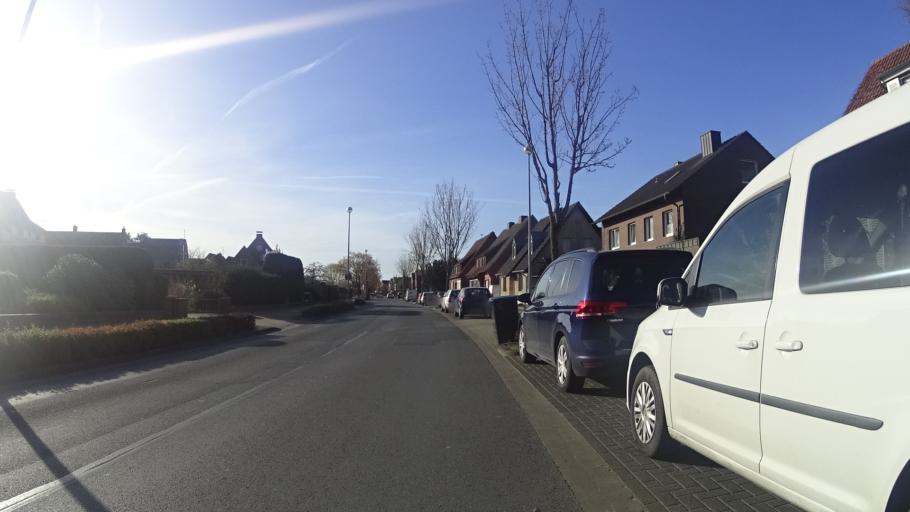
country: DE
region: North Rhine-Westphalia
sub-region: Regierungsbezirk Munster
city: Greven
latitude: 52.1002
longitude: 7.5887
